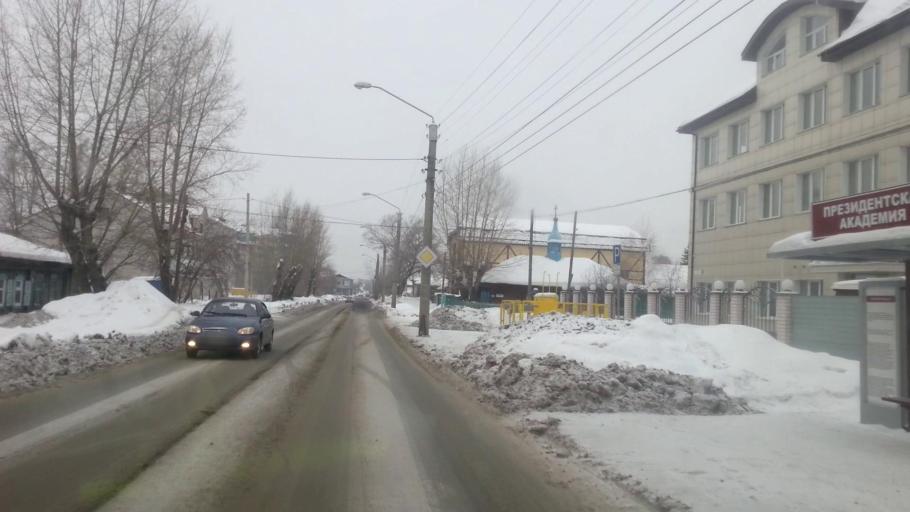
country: RU
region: Altai Krai
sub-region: Gorod Barnaulskiy
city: Barnaul
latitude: 53.3319
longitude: 83.7652
